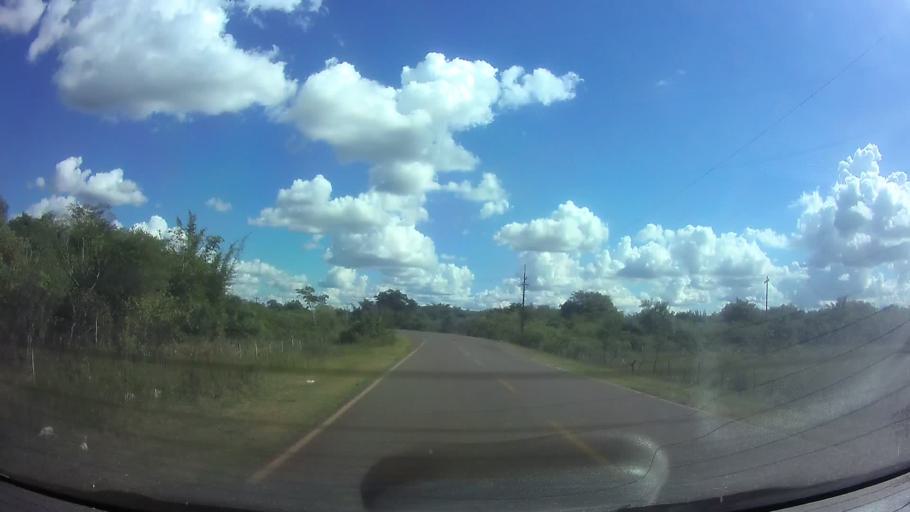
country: PY
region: Paraguari
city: Sapucai
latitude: -25.6830
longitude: -56.8634
